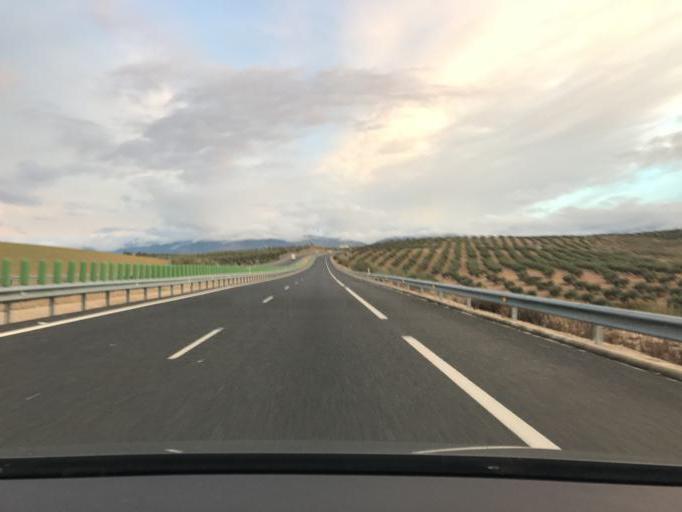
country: ES
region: Andalusia
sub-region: Provincia de Jaen
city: Jaen
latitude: 37.8194
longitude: -3.7423
